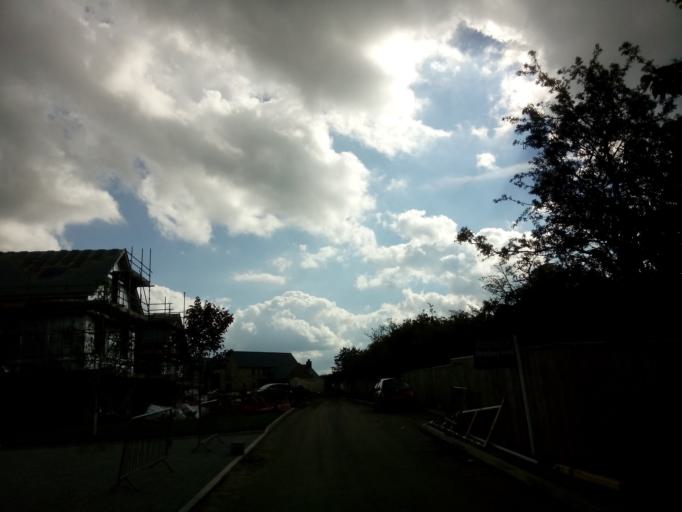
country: GB
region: England
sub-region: County Durham
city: West Rainton
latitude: 54.7914
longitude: -1.5189
